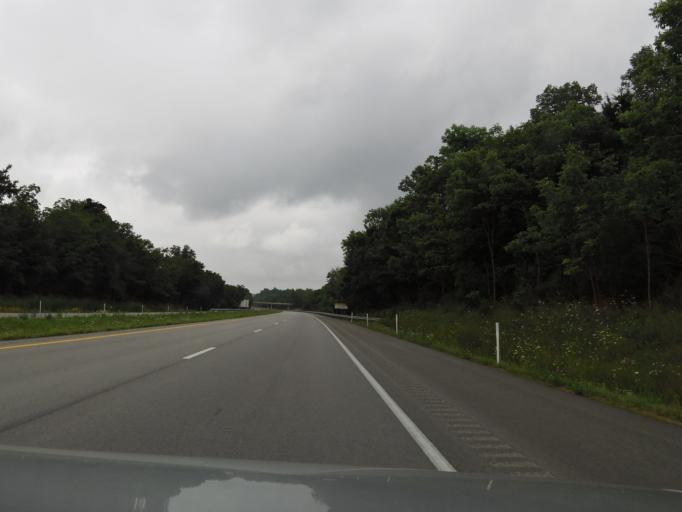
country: US
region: Kentucky
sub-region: Grayson County
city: Leitchfield
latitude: 37.4085
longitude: -86.4661
